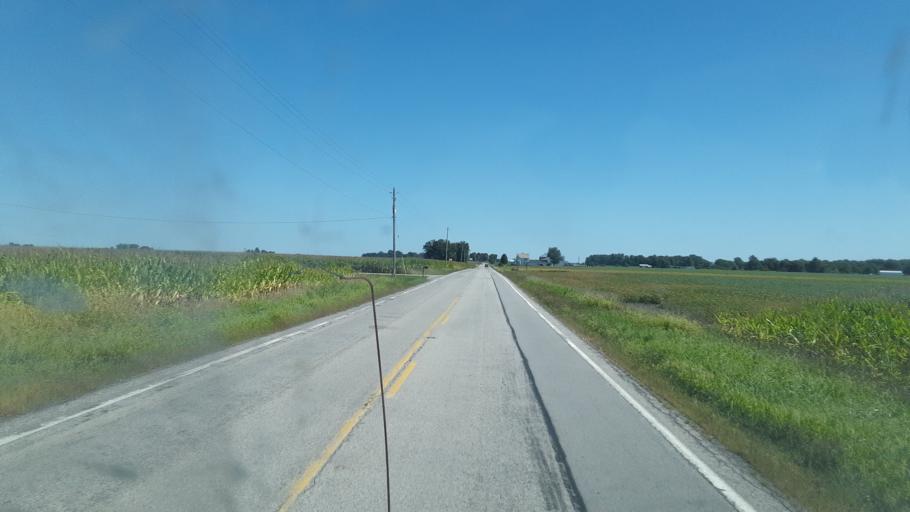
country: US
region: Ohio
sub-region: Huron County
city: Bellevue
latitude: 41.2213
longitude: -82.7788
